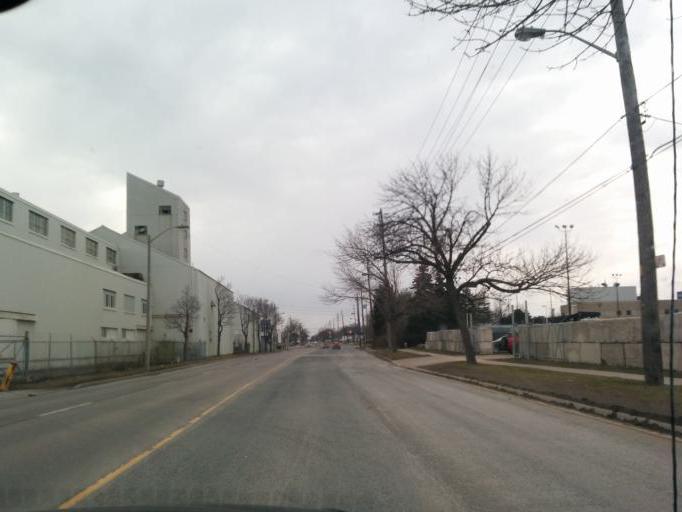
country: CA
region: Ontario
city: Etobicoke
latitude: 43.6078
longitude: -79.5180
